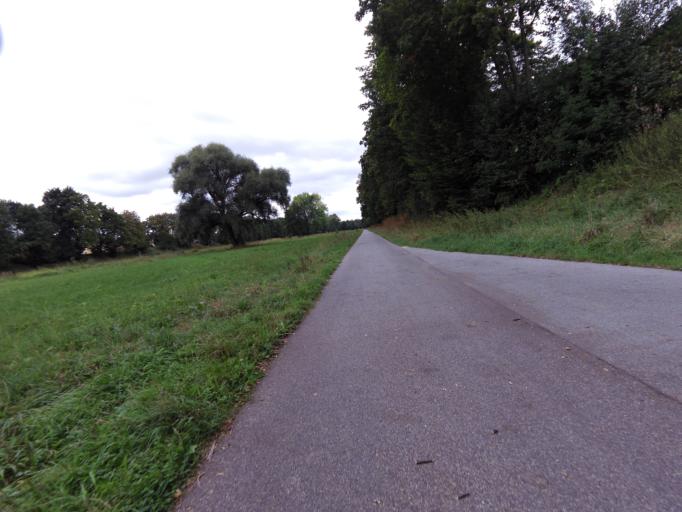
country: DE
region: Bavaria
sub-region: Lower Bavaria
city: Landshut
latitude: 48.5458
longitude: 12.1349
